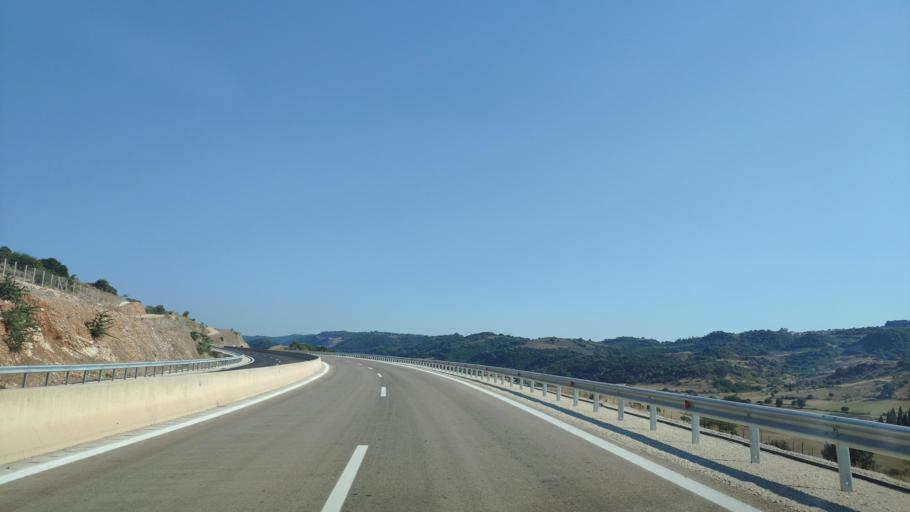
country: GR
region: West Greece
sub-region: Nomos Aitolias kai Akarnanias
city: Katouna
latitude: 38.8108
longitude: 21.1288
